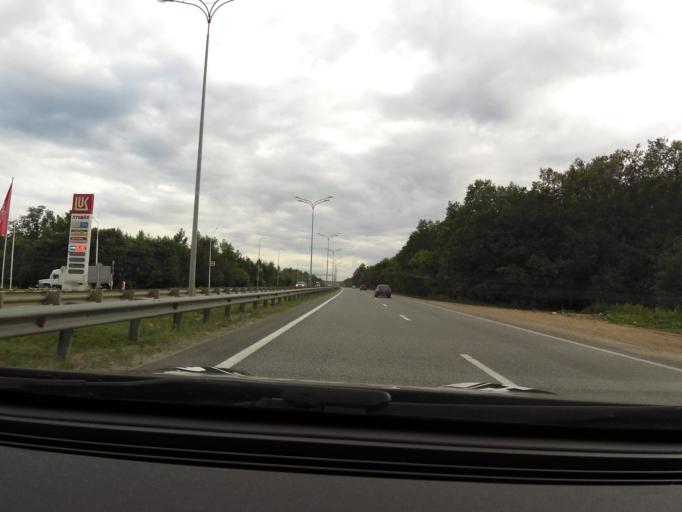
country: RU
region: Tatarstan
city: Sviyazhsk
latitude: 55.7523
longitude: 48.8031
